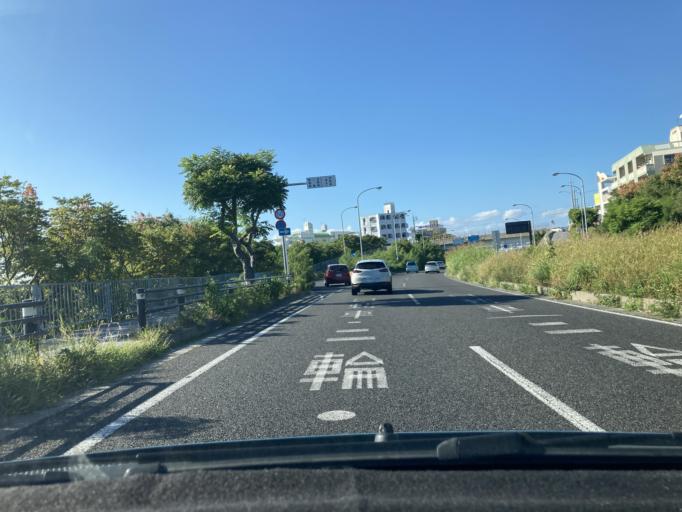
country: JP
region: Okinawa
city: Ginowan
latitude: 26.2501
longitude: 127.7425
